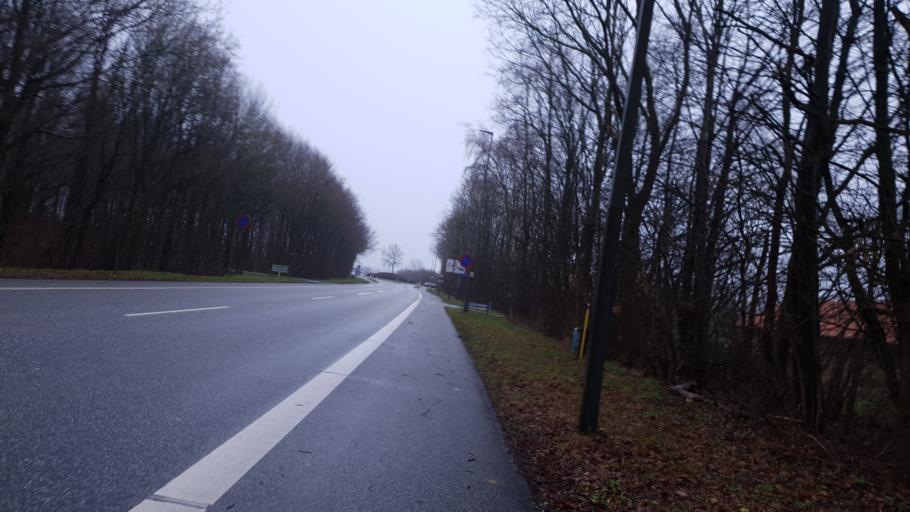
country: DK
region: Central Jutland
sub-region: Hedensted Kommune
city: Hedensted
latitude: 55.7829
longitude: 9.6974
